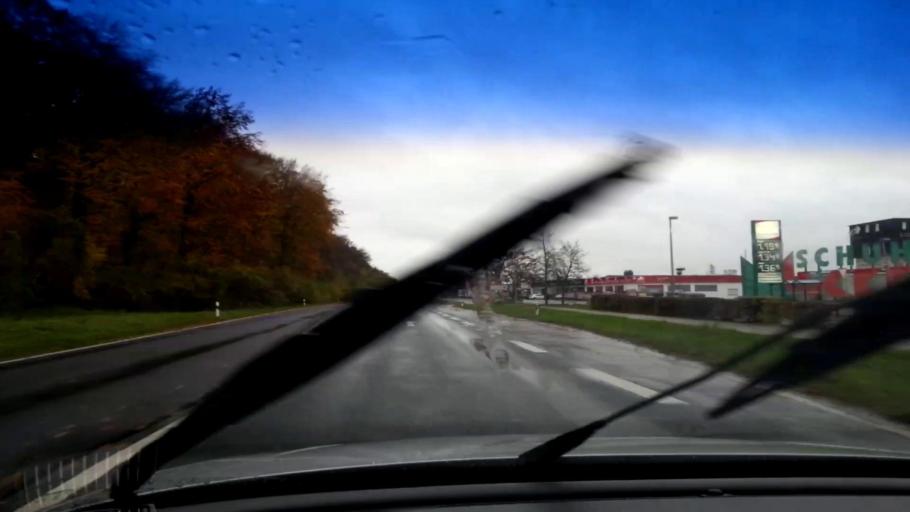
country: DE
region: Bavaria
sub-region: Upper Franconia
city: Oberhaid
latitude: 49.9174
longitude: 10.8076
